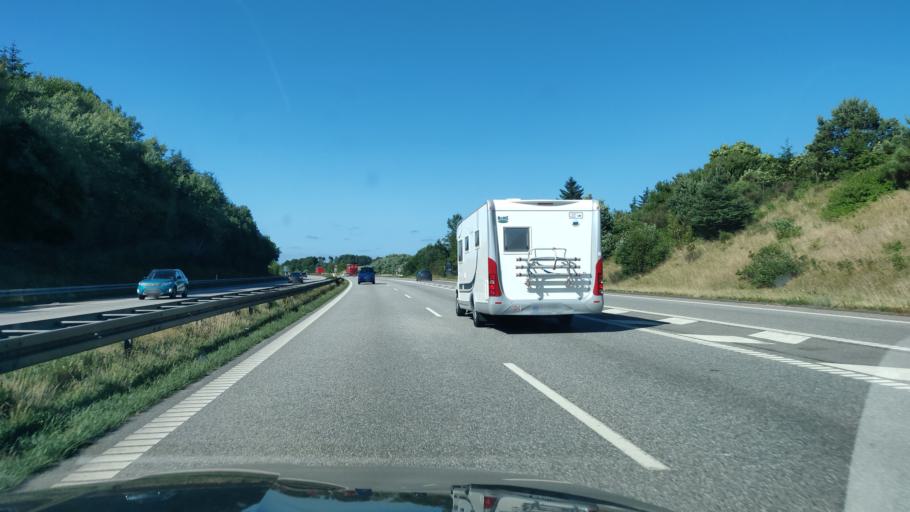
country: DK
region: North Denmark
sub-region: Rebild Kommune
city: Stovring
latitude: 56.9090
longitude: 9.8388
